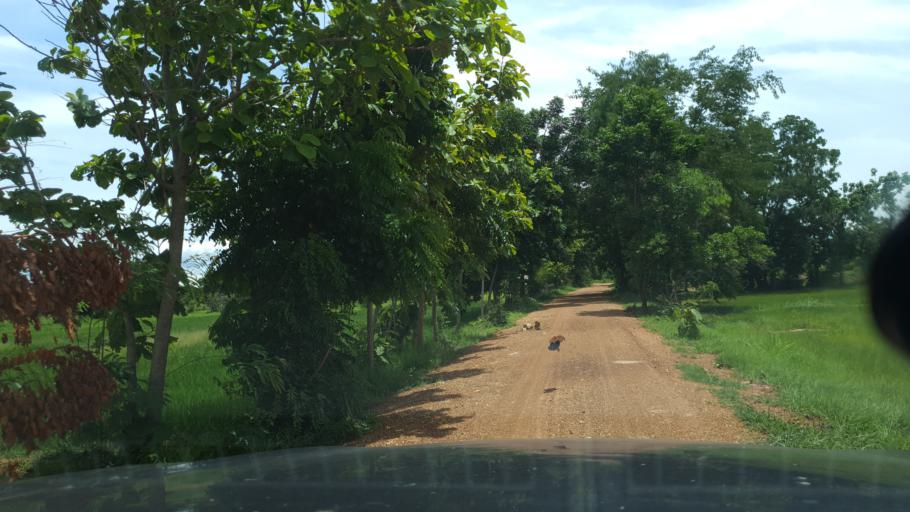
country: TH
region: Sukhothai
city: Ban Na
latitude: 17.0730
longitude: 99.6973
